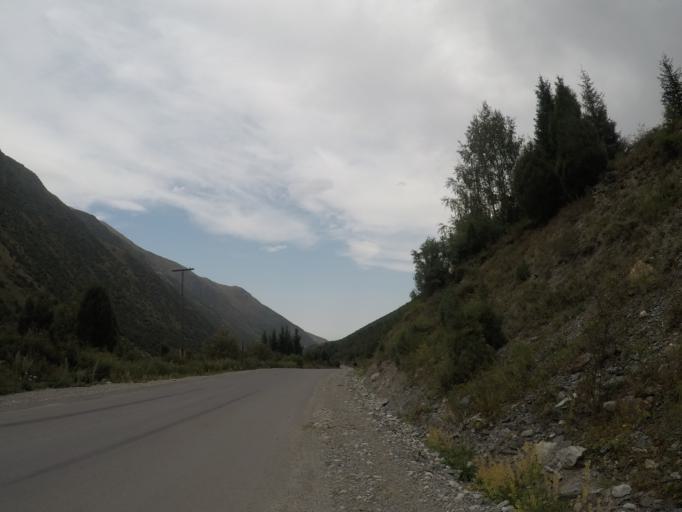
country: KG
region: Chuy
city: Bishkek
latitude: 42.5848
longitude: 74.4838
